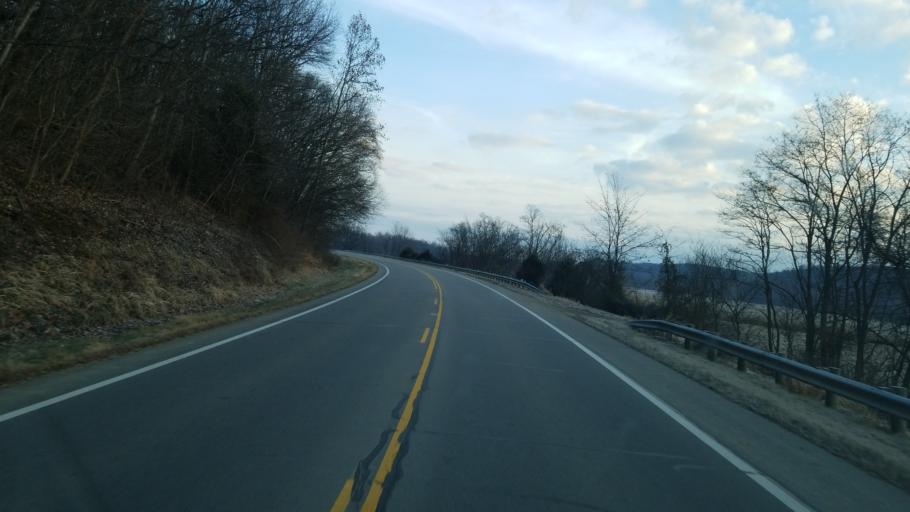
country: US
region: Ohio
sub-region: Ross County
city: North Fork Village
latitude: 39.3191
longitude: -83.1047
